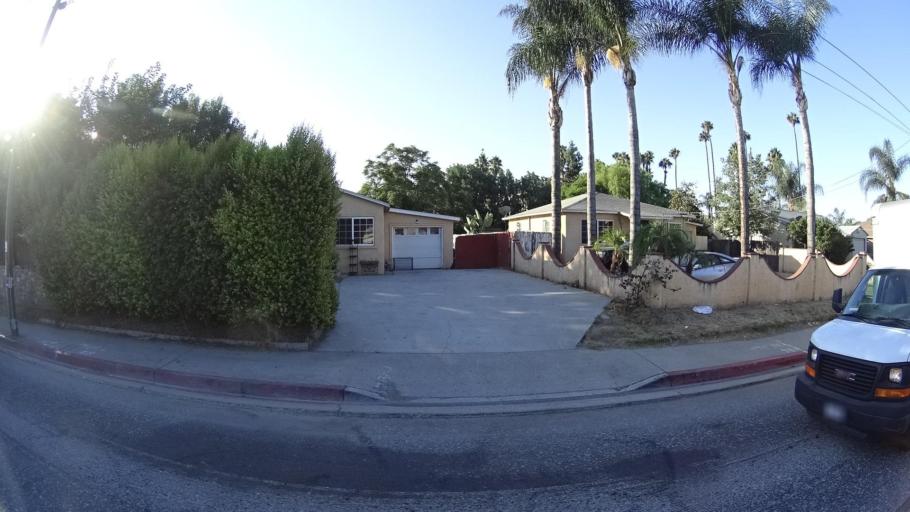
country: US
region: California
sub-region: San Diego County
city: Escondido
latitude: 33.1294
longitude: -117.0761
